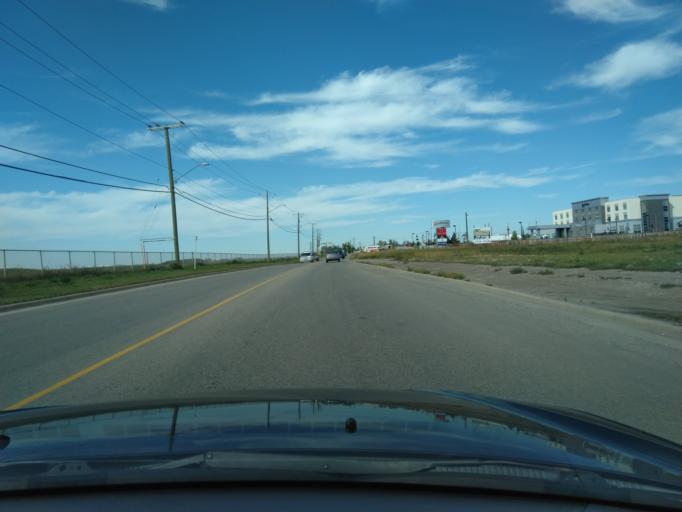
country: CA
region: Alberta
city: Calgary
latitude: 51.1102
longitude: -113.9821
